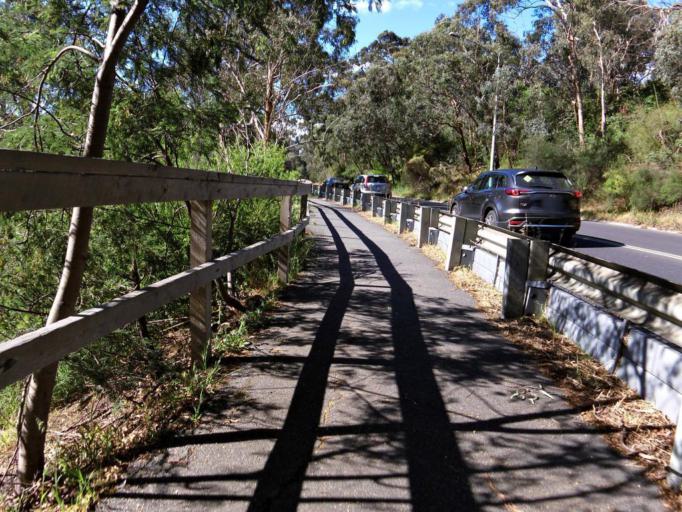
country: AU
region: Victoria
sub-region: Nillumbik
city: Eltham
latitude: -37.7301
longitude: 145.1450
